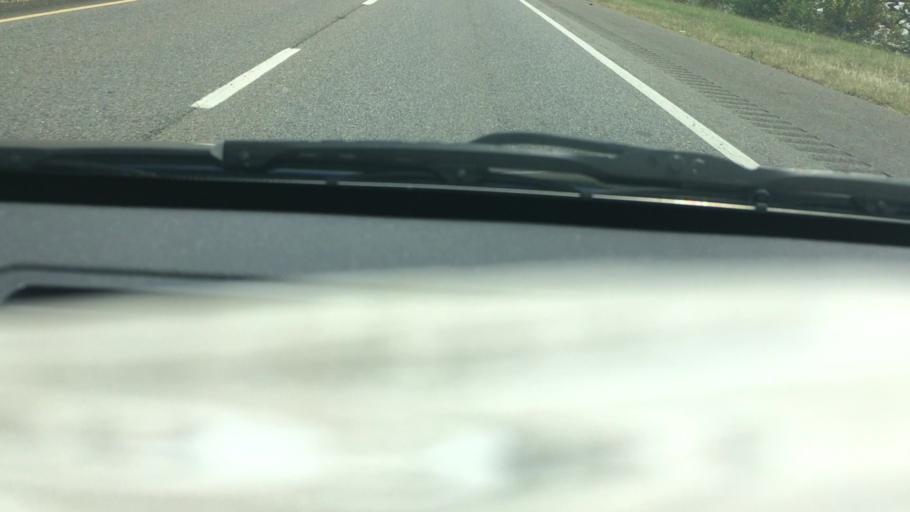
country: US
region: Alabama
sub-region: Pickens County
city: Gordo
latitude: 33.2792
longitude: -87.7826
